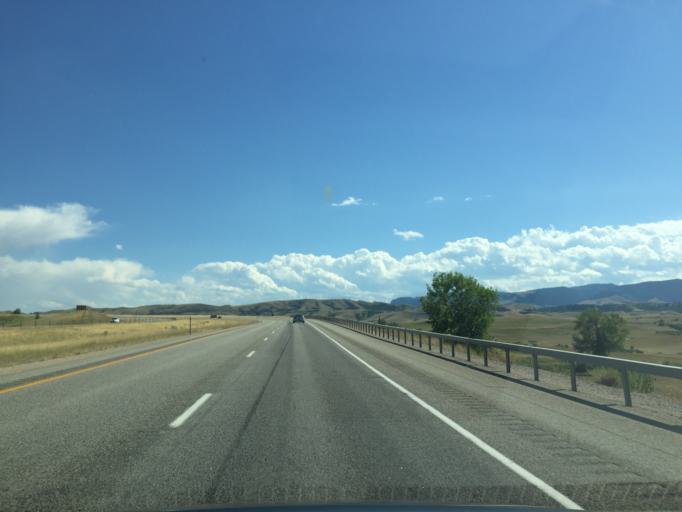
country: US
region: Wyoming
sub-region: Sheridan County
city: Sheridan
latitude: 44.6088
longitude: -106.8476
